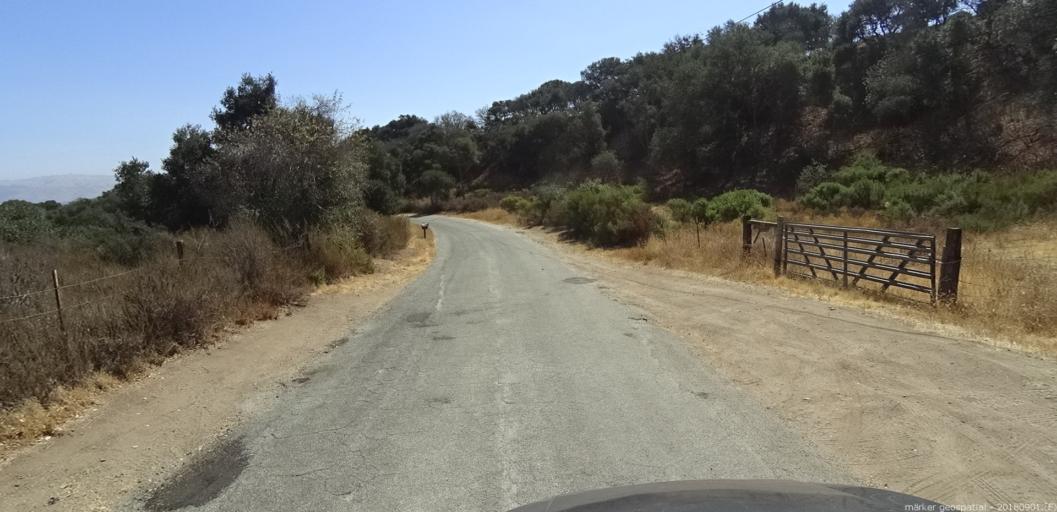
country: US
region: California
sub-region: Monterey County
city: Chualar
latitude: 36.5100
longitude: -121.5308
